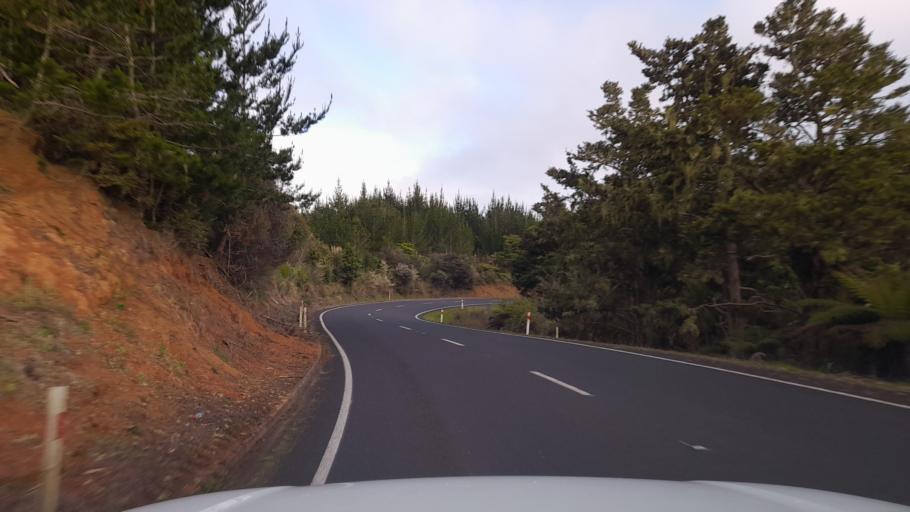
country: NZ
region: Northland
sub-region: Far North District
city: Waimate North
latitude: -35.5098
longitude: 173.8372
